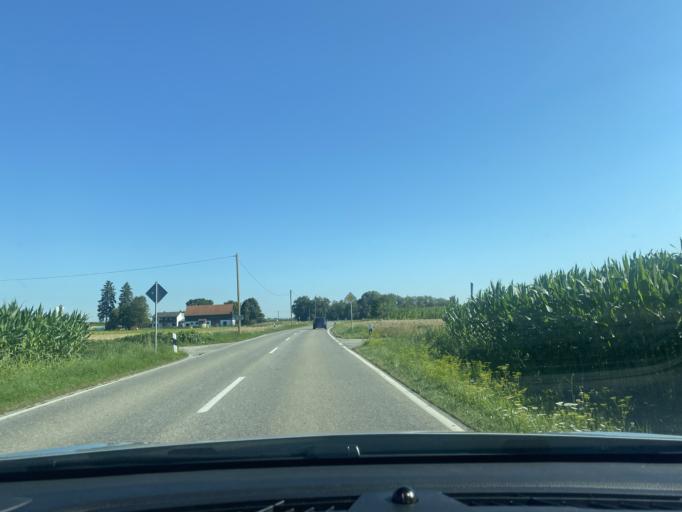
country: DE
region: Bavaria
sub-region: Upper Bavaria
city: Erding
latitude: 48.3213
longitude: 11.8938
